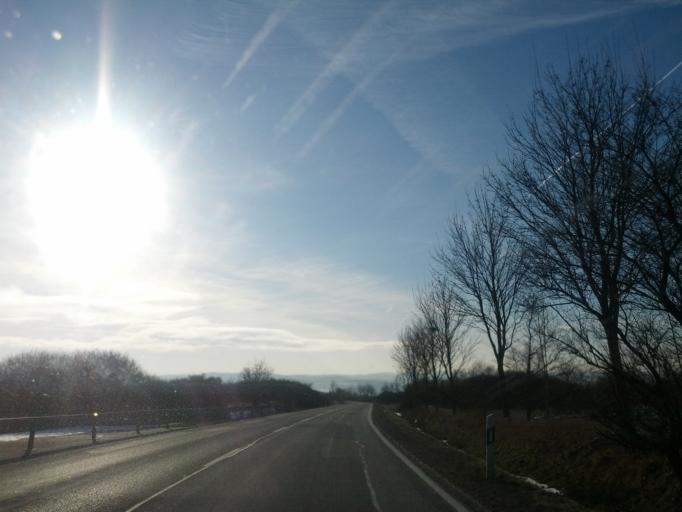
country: DE
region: Thuringia
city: Haina
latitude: 51.0077
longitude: 10.4492
